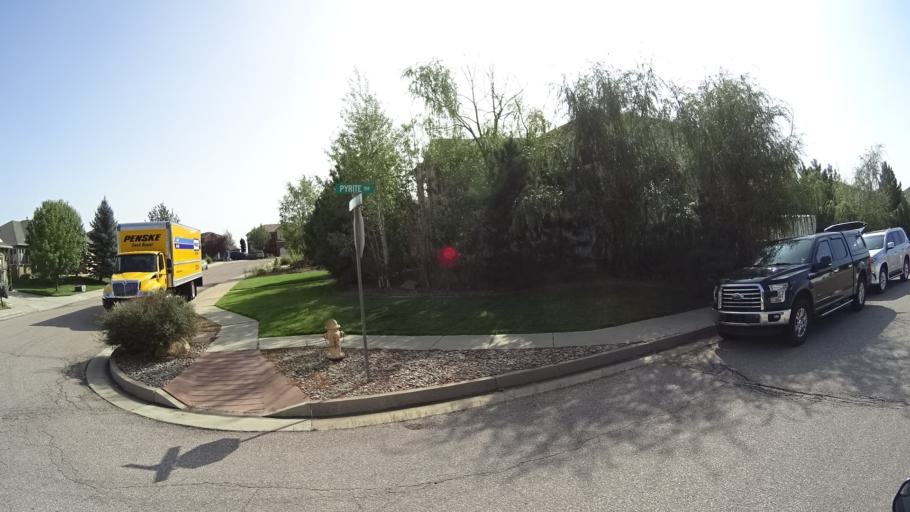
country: US
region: Colorado
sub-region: El Paso County
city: Colorado Springs
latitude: 38.8291
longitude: -104.8495
